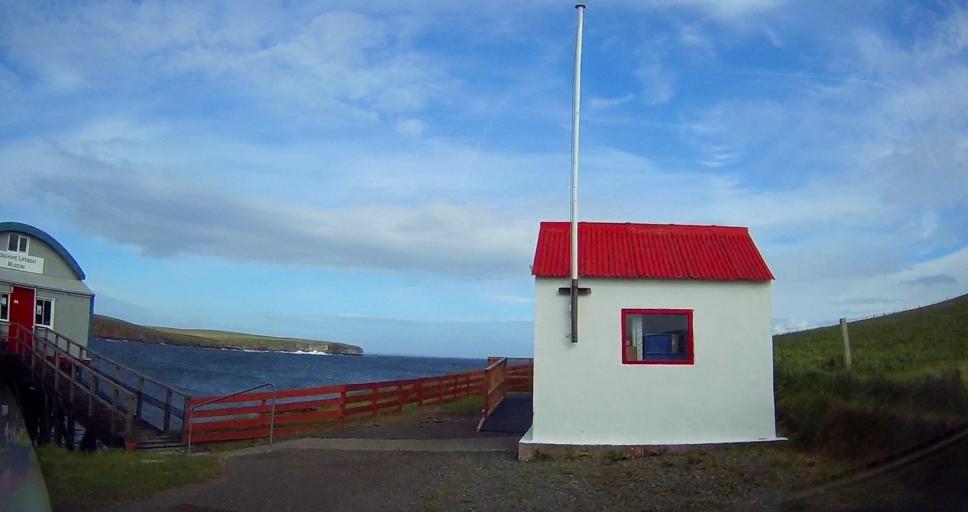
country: GB
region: Scotland
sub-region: Orkney Islands
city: Stromness
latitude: 58.7797
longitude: -3.2286
